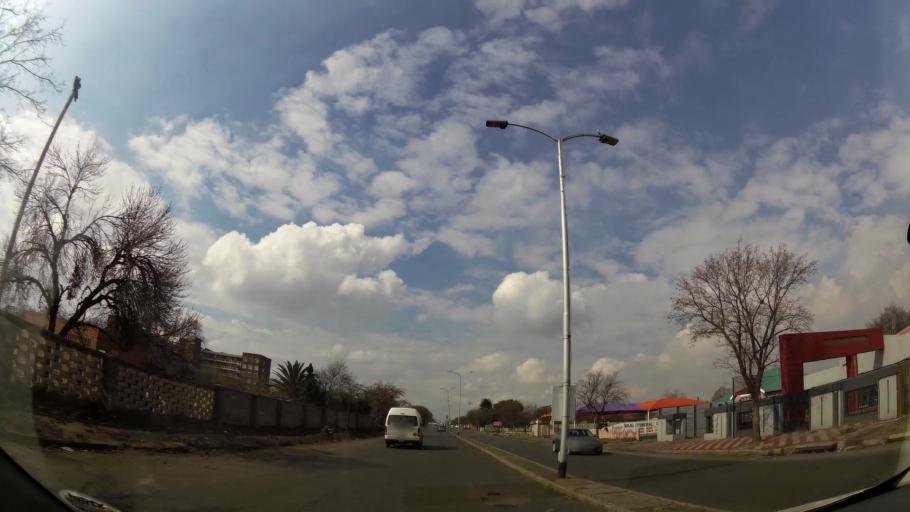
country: ZA
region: Gauteng
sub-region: Sedibeng District Municipality
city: Vereeniging
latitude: -26.6748
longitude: 27.9226
